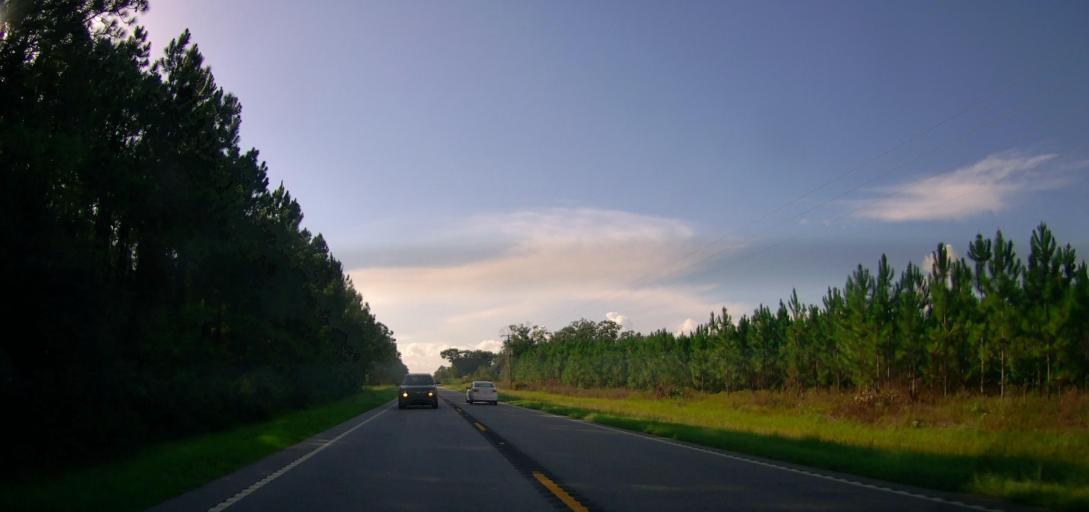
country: US
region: Georgia
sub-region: Coffee County
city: Nicholls
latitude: 31.4274
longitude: -82.7001
